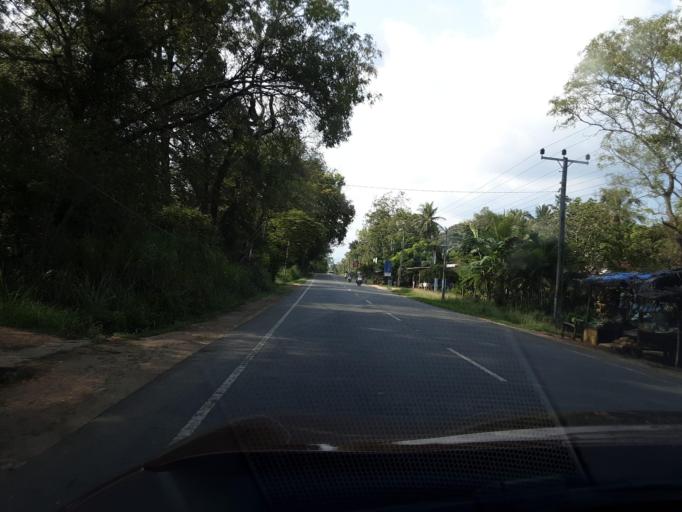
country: LK
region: Uva
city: Haputale
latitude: 6.6648
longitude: 81.1138
